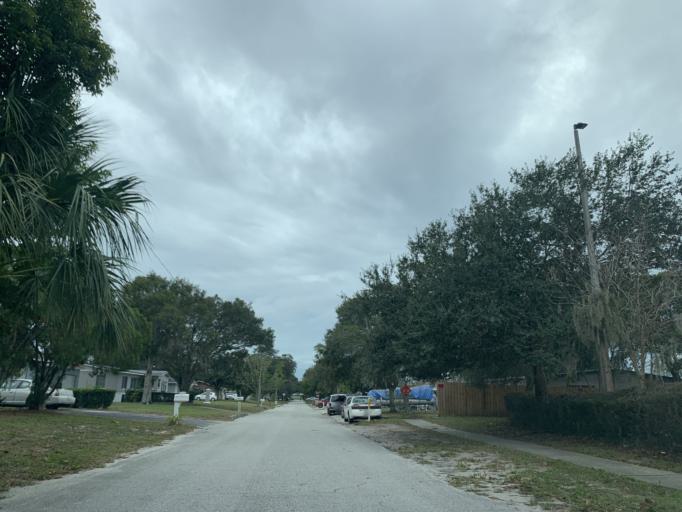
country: US
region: Florida
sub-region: Pinellas County
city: Belleair
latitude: 27.9384
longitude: -82.7863
